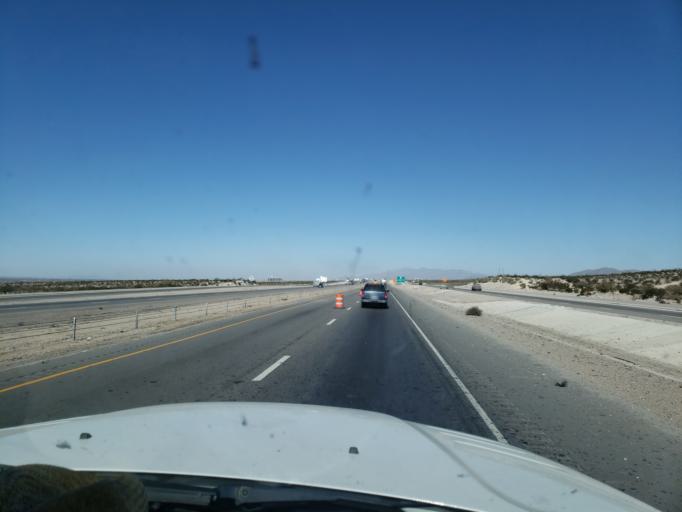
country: US
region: Texas
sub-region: El Paso County
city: Westway
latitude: 31.9325
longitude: -106.5827
